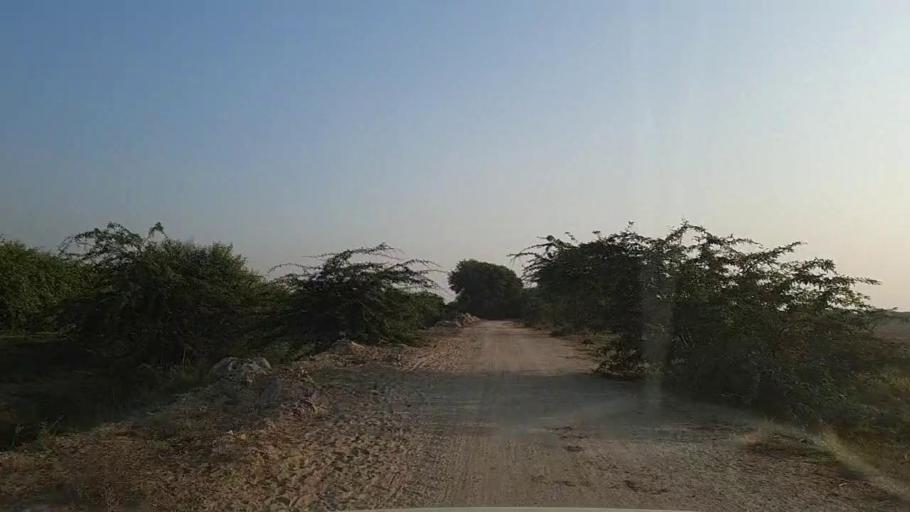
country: PK
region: Sindh
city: Daro Mehar
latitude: 24.7425
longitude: 68.1844
